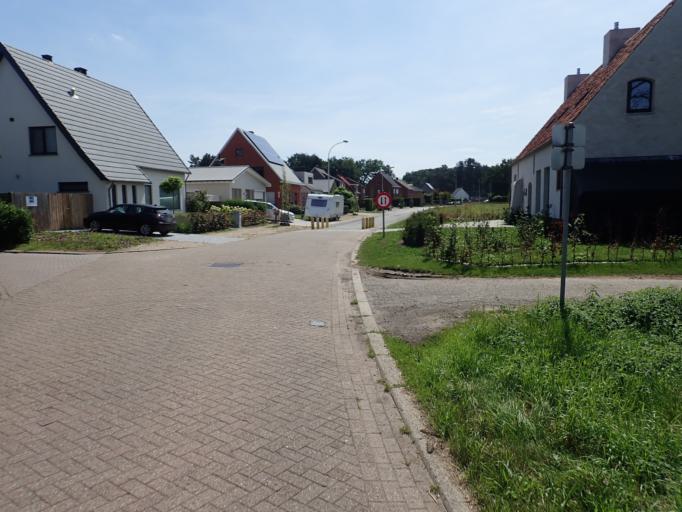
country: BE
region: Flanders
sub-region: Provincie Antwerpen
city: Zandhoven
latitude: 51.2190
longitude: 4.6521
